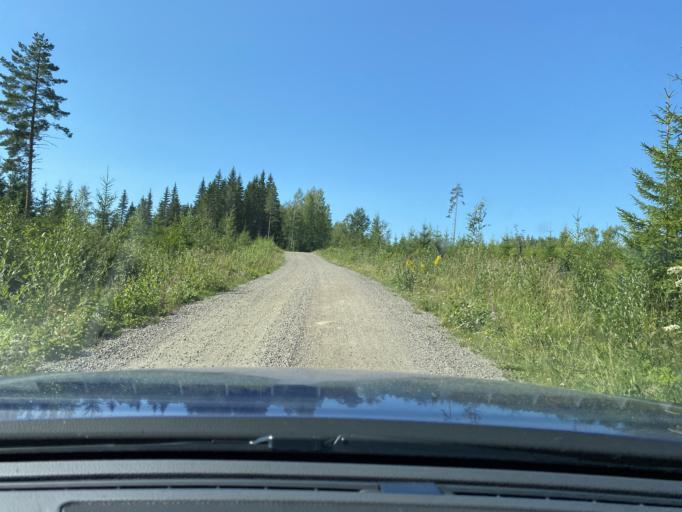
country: FI
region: Central Finland
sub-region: Jaemsae
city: Jaemsae
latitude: 61.8477
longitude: 25.3789
